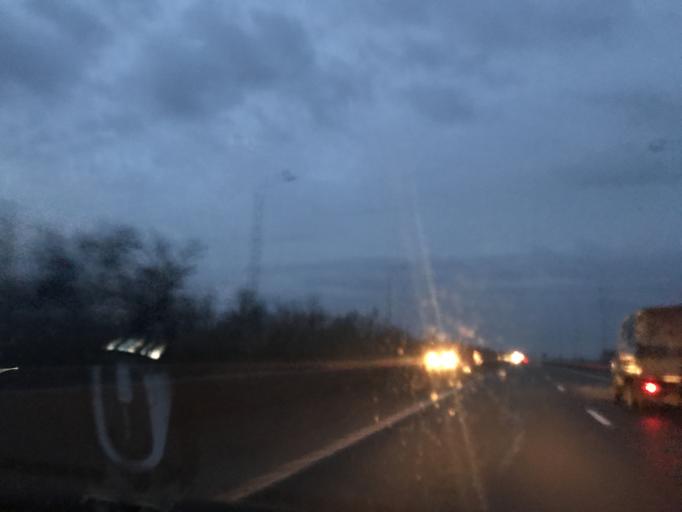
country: RU
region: Rostov
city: Samarskoye
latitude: 46.9807
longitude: 39.7237
